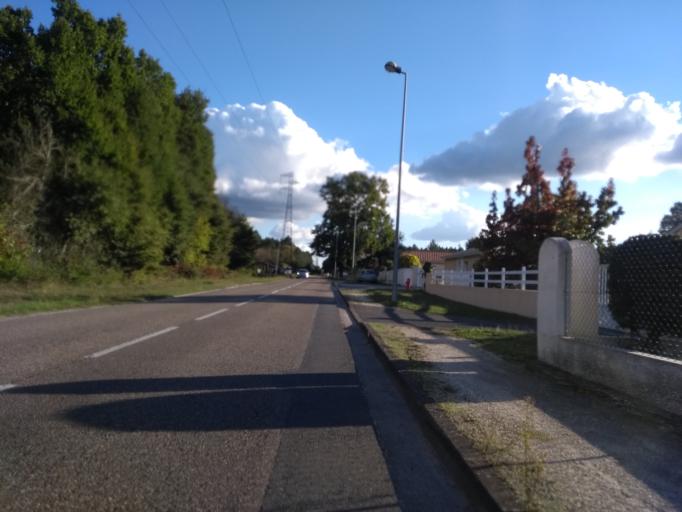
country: FR
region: Aquitaine
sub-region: Departement de la Gironde
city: Canejan
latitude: 44.7471
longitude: -0.6376
